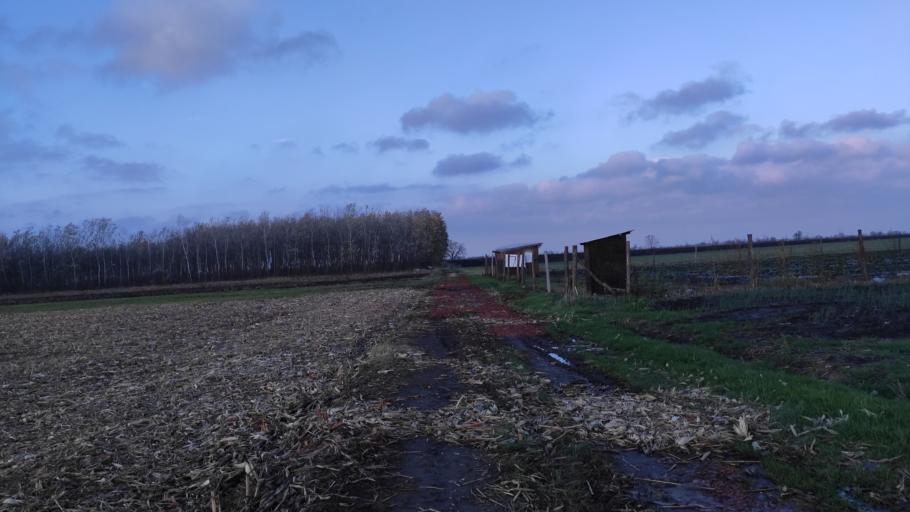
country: HU
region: Bekes
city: Mezobereny
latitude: 46.7628
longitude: 21.0518
